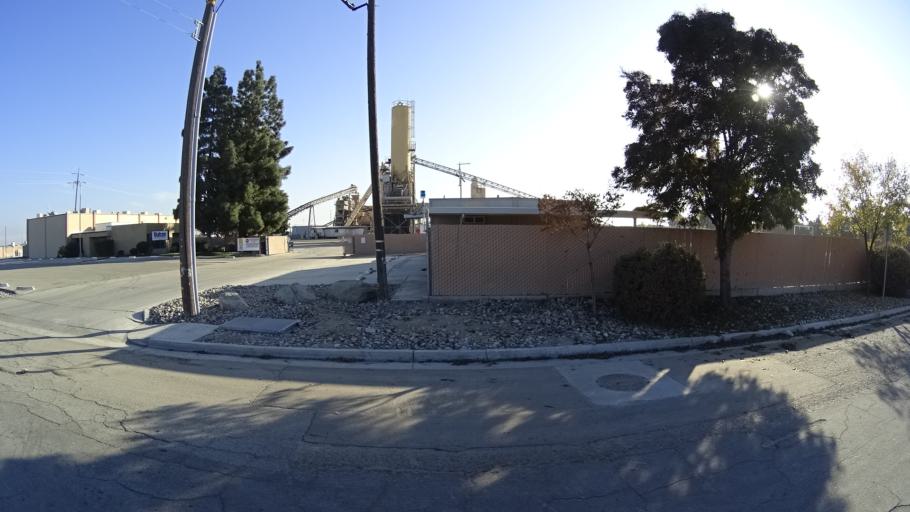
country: US
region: California
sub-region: Kern County
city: Greenacres
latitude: 35.2961
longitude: -119.0976
